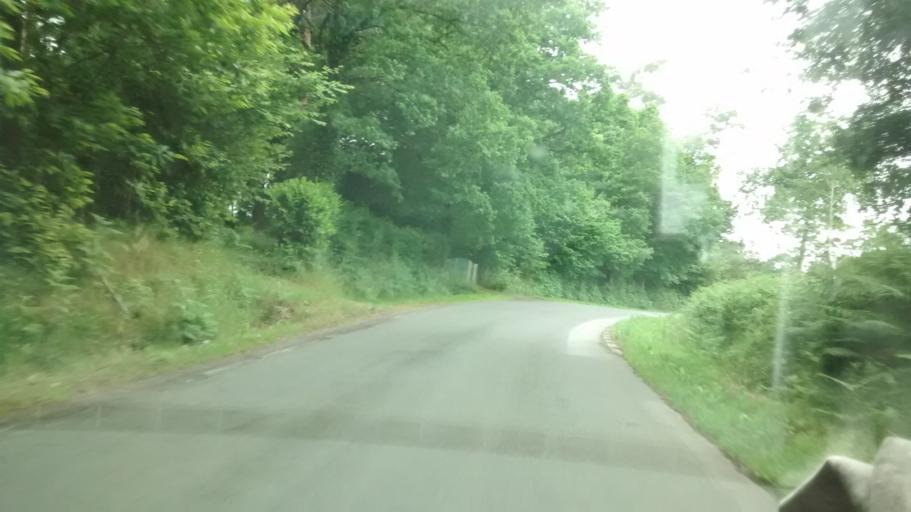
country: FR
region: Brittany
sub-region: Departement du Morbihan
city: Molac
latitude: 47.7160
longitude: -2.4347
